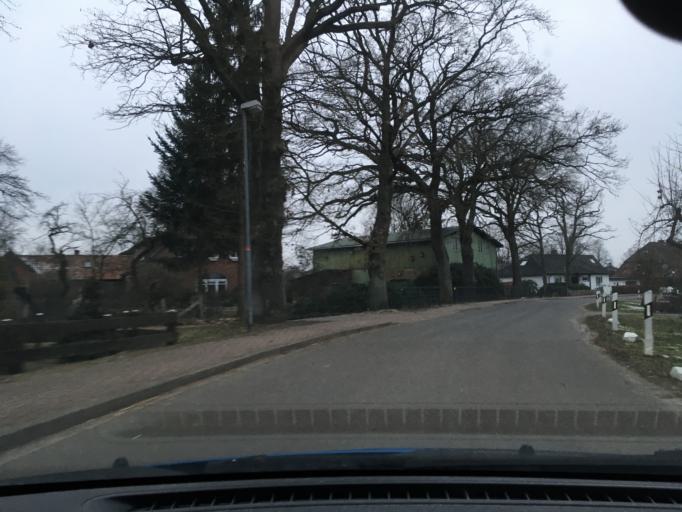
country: DE
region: Lower Saxony
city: Stelle
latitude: 53.3619
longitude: 10.1469
